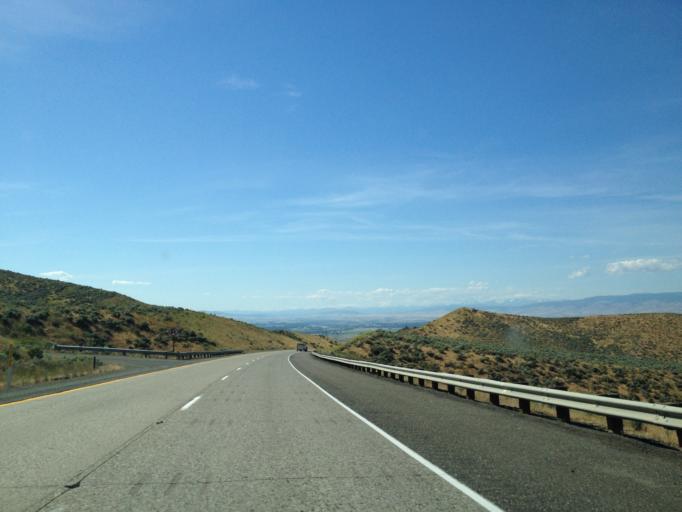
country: US
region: Washington
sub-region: Kittitas County
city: Kittitas
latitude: 46.8951
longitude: -120.4451
